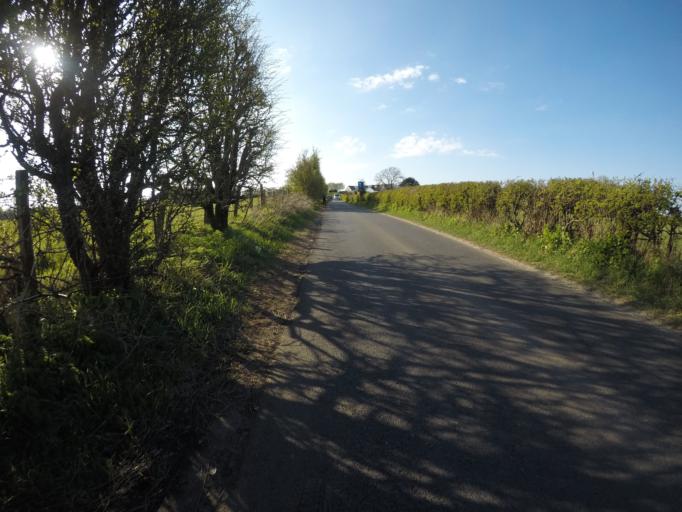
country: GB
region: Scotland
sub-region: North Ayrshire
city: Stevenston
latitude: 55.6495
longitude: -4.7312
